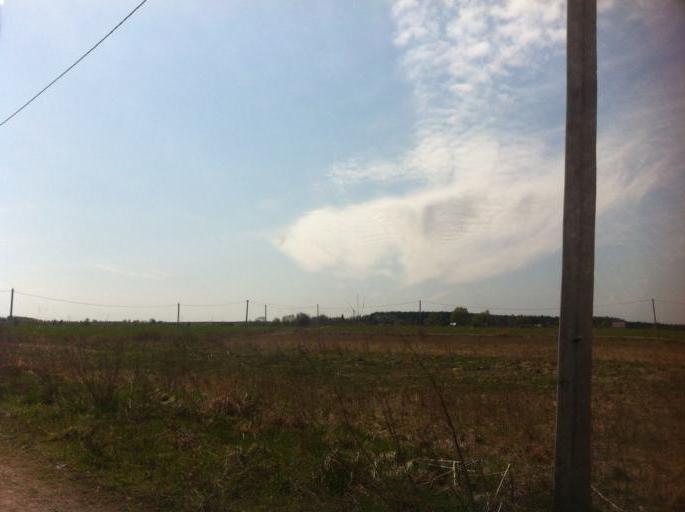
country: RU
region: Pskov
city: Izborsk
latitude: 57.8223
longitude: 27.9649
